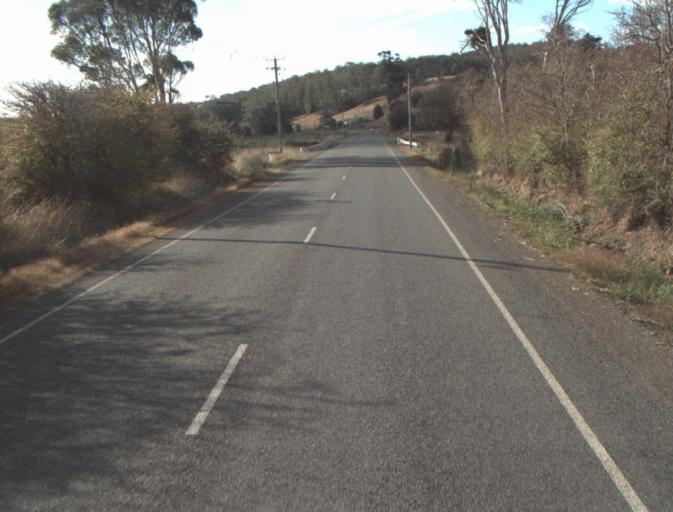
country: AU
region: Tasmania
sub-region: Launceston
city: Mayfield
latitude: -41.2431
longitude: 147.2167
